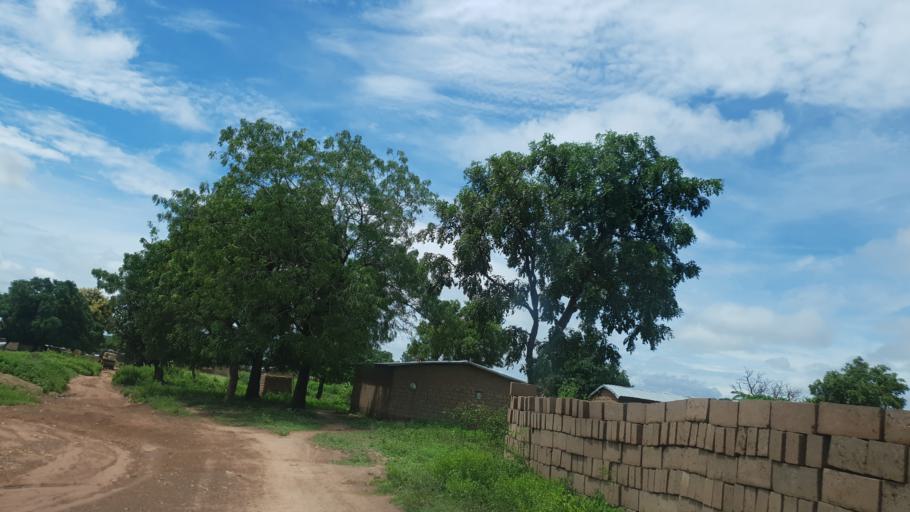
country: CI
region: Savanes
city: Tengrela
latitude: 10.3620
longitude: -6.9195
